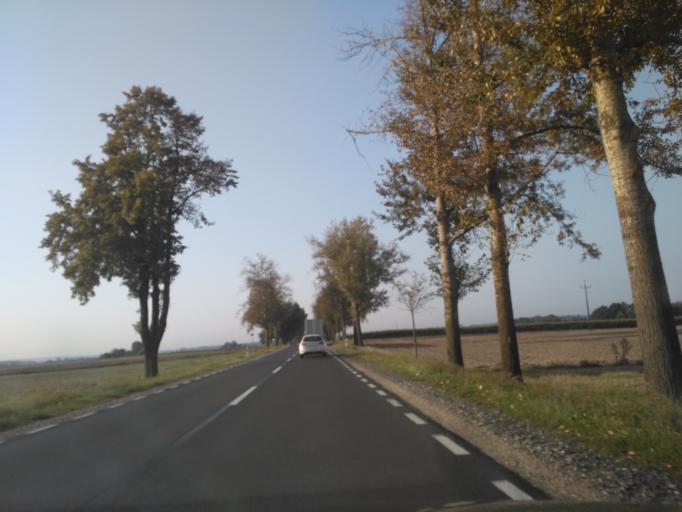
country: PL
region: Lublin Voivodeship
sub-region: Powiat krasnicki
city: Szastarka
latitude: 50.8132
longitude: 22.3193
